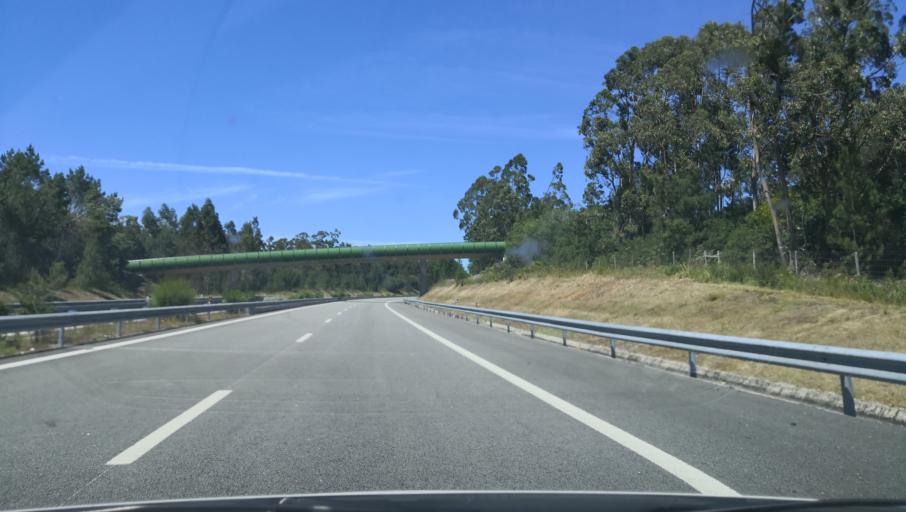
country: PT
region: Coimbra
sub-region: Montemor-O-Velho
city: Montemor-o-Velho
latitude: 40.2160
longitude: -8.6752
